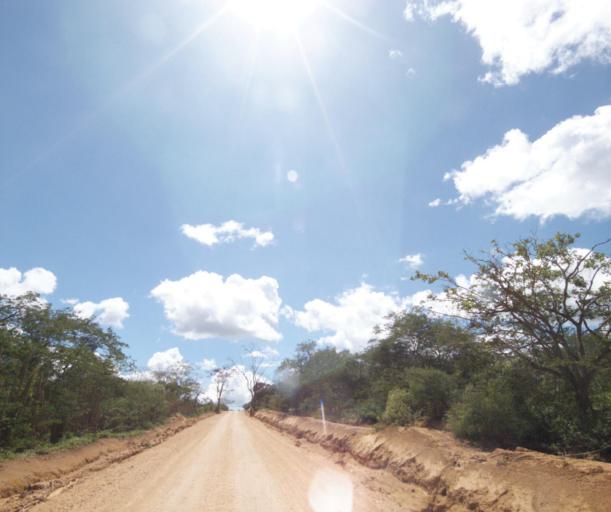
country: BR
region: Bahia
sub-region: Pocoes
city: Pocoes
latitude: -14.2993
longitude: -40.6512
